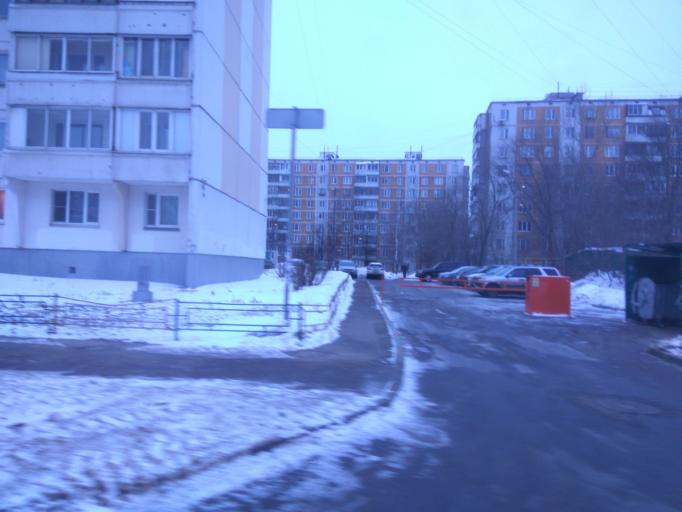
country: RU
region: Moscow
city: Gol'yanovo
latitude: 55.8140
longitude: 37.8282
